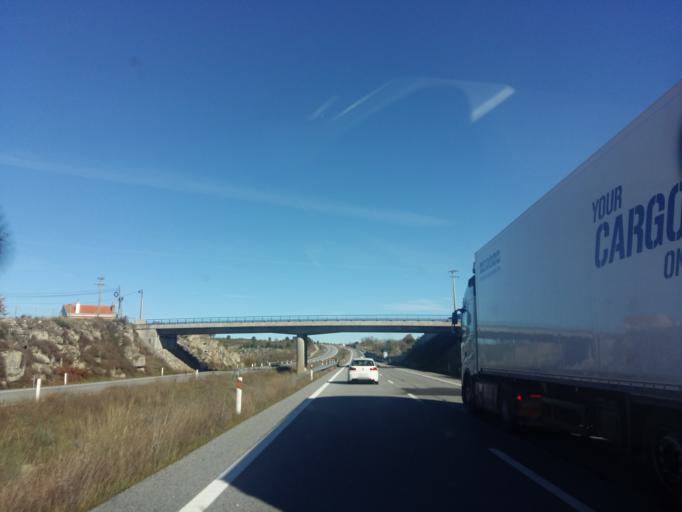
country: PT
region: Guarda
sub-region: Guarda
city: Sequeira
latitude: 40.5854
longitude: -7.1514
